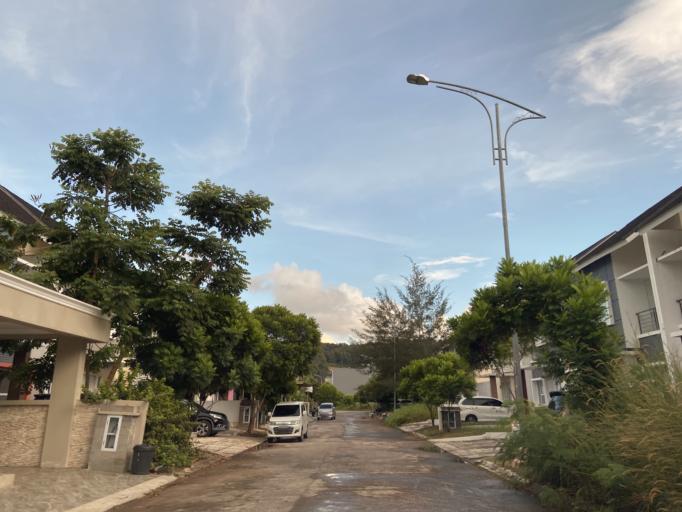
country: SG
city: Singapore
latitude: 1.0899
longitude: 104.0329
